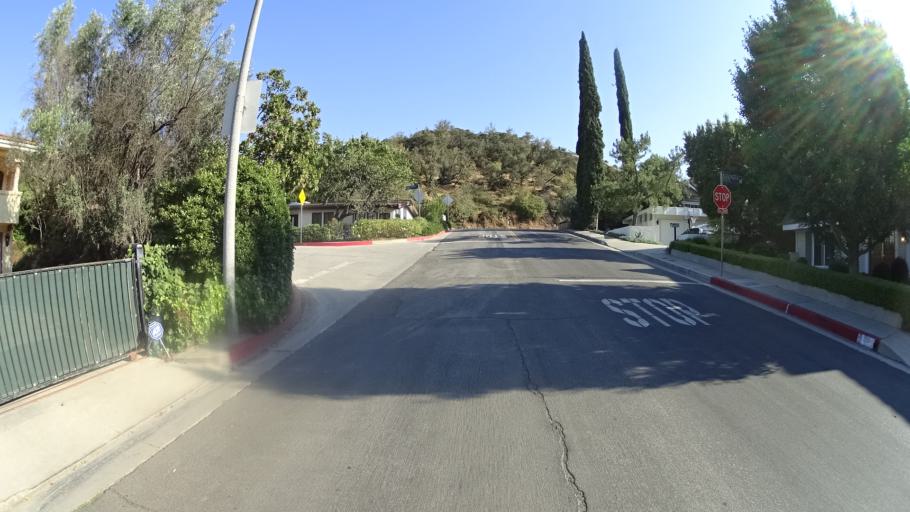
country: US
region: California
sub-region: Los Angeles County
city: Universal City
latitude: 34.1272
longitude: -118.3873
